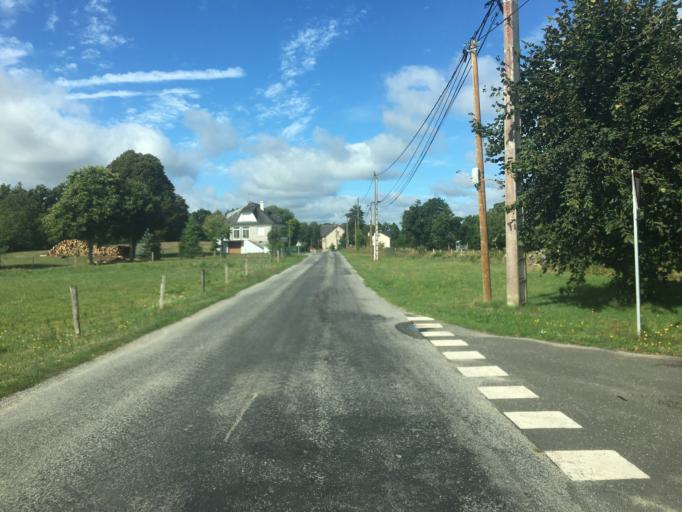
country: FR
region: Auvergne
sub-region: Departement du Cantal
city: Champagnac
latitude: 45.4159
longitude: 2.4113
